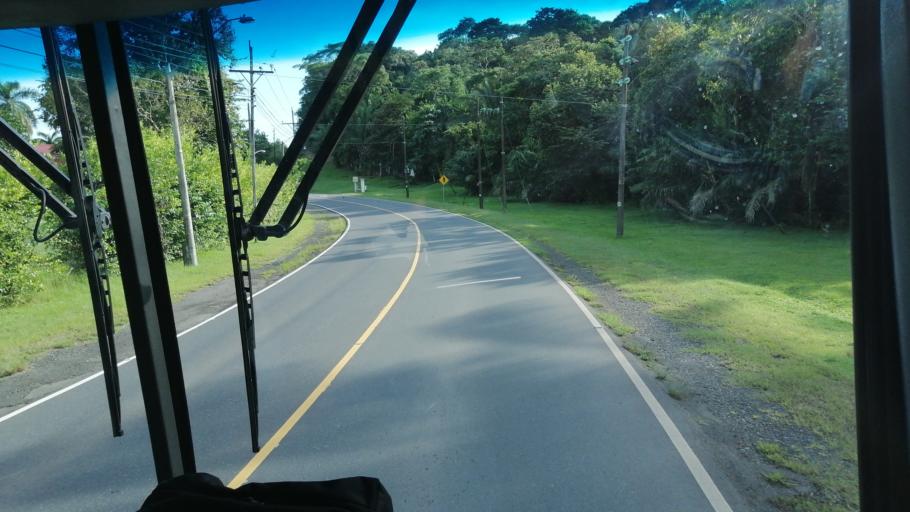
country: PA
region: Panama
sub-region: Distrito de Panama
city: Ancon
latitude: 8.9465
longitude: -79.5915
